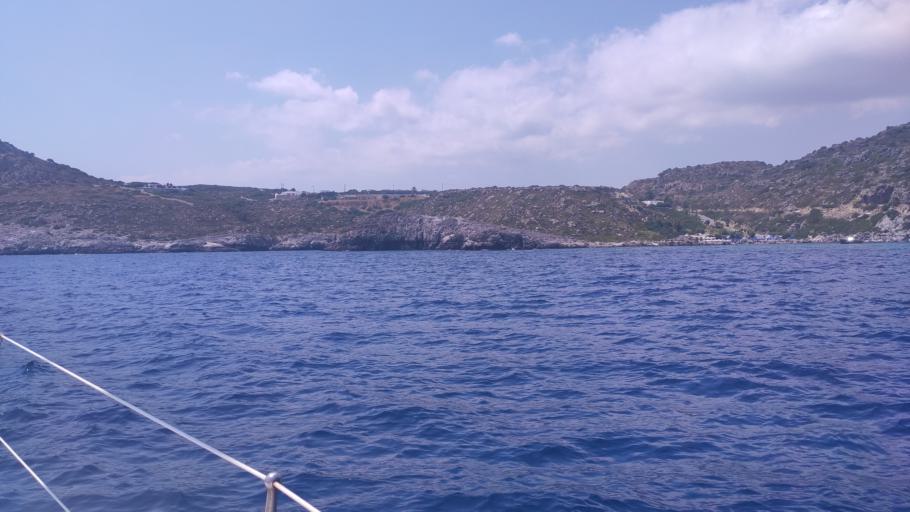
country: GR
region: South Aegean
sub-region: Nomos Dodekanisou
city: Faliraki
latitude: 36.3183
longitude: 28.2095
